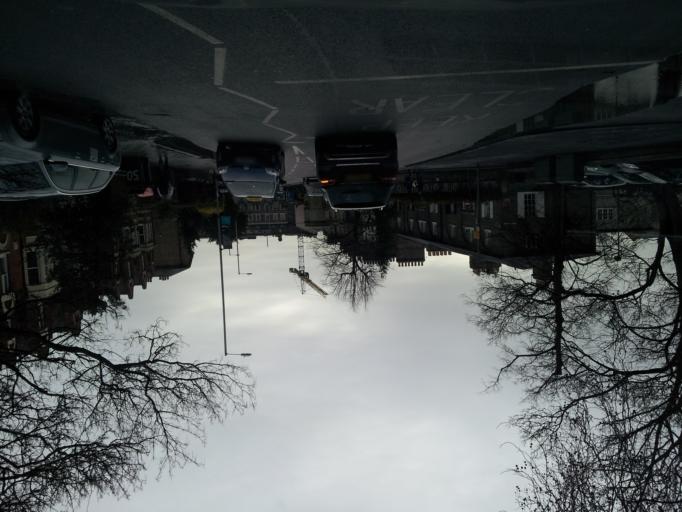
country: GB
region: England
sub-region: Cambridgeshire
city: Cambridge
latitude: 52.1982
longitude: 0.1248
